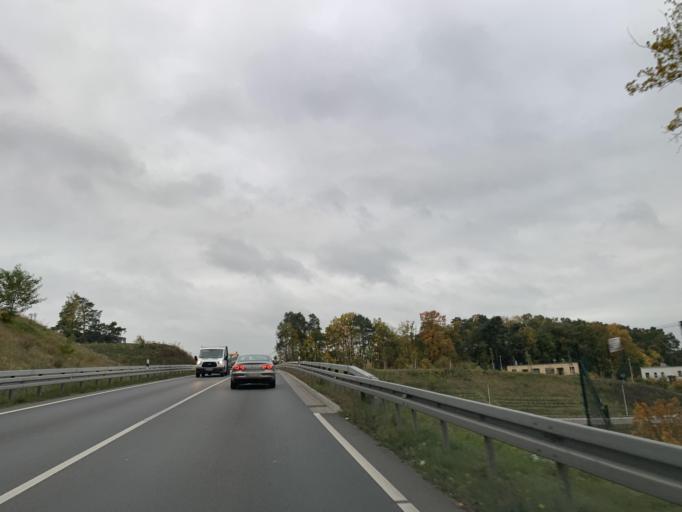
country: DE
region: Mecklenburg-Vorpommern
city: Neubrandenburg
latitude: 53.5427
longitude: 13.2738
